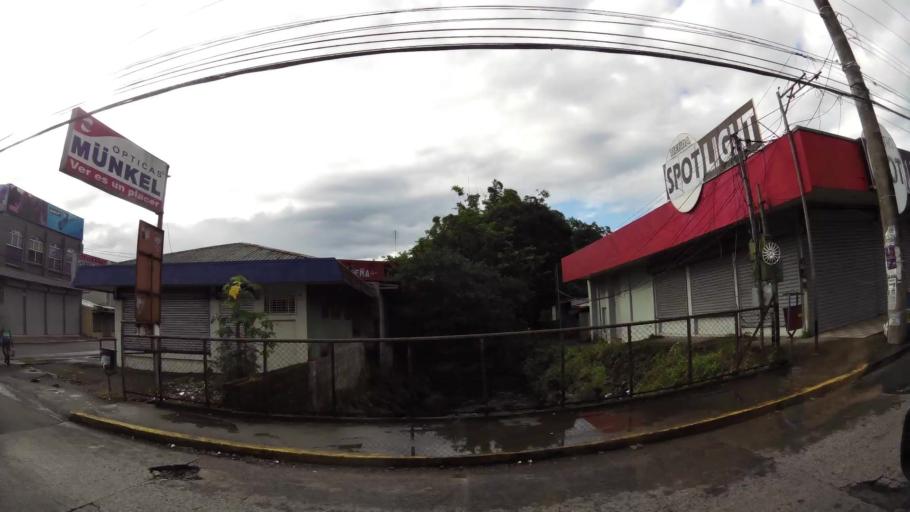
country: CR
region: Limon
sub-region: Canton de Pococi
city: Guapiles
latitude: 10.2159
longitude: -83.7862
